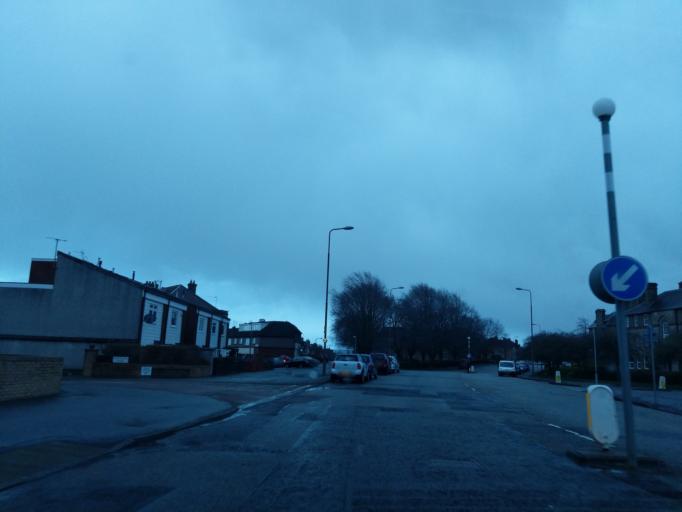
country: GB
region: Scotland
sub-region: West Lothian
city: Seafield
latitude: 55.9529
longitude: -3.1380
